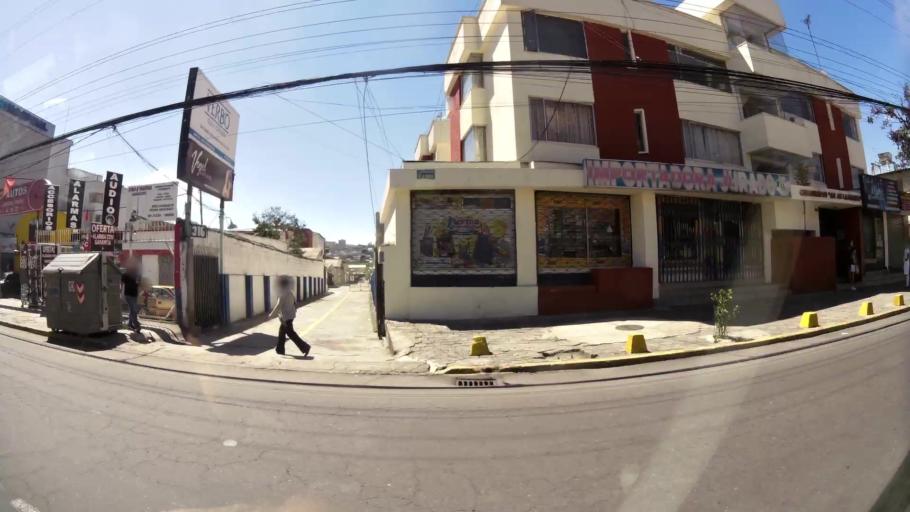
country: EC
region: Pichincha
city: Quito
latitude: -0.1301
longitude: -78.4939
